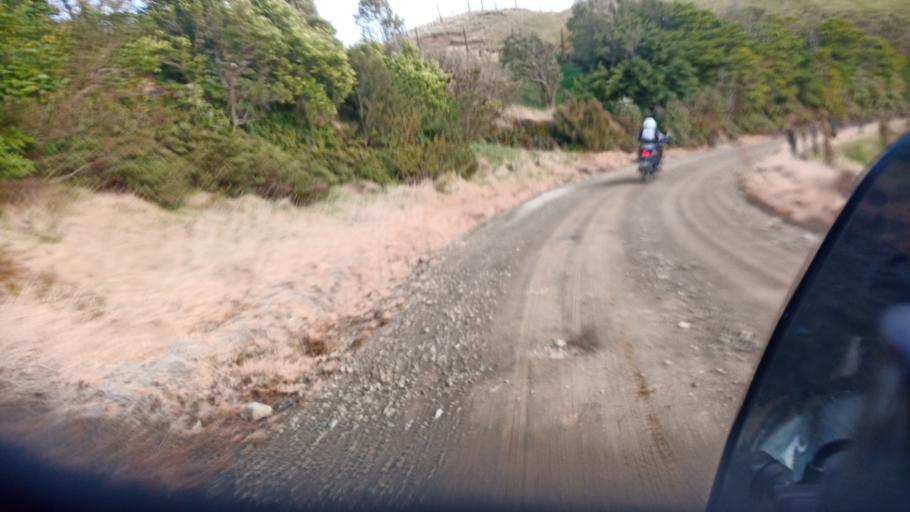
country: NZ
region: Gisborne
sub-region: Gisborne District
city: Gisborne
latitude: -38.4758
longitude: 177.5180
